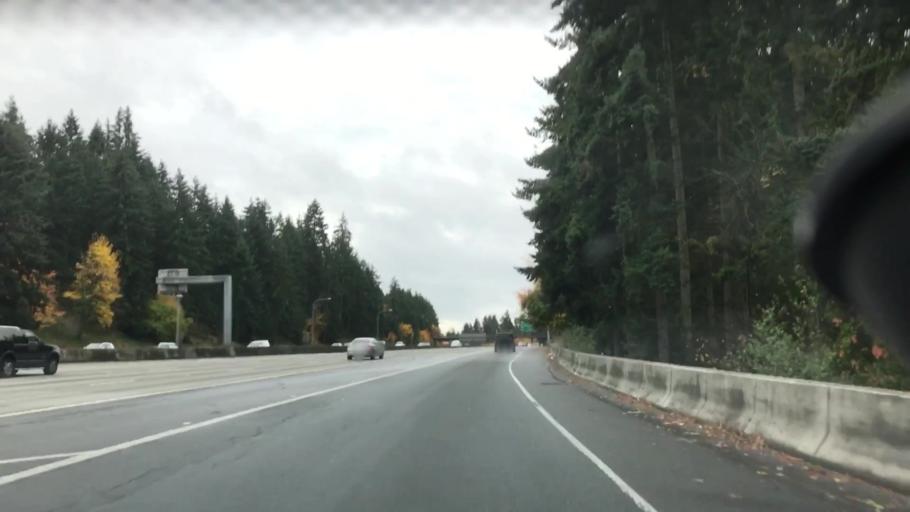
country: US
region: Washington
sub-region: Snohomish County
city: Mountlake Terrace
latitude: 47.7737
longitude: -122.3195
